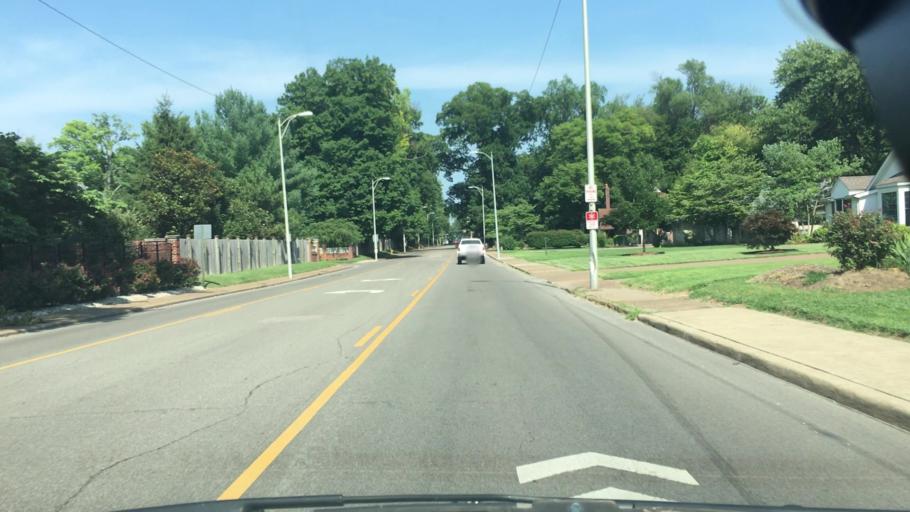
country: US
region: Indiana
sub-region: Vanderburgh County
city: Evansville
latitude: 37.9699
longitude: -87.5243
